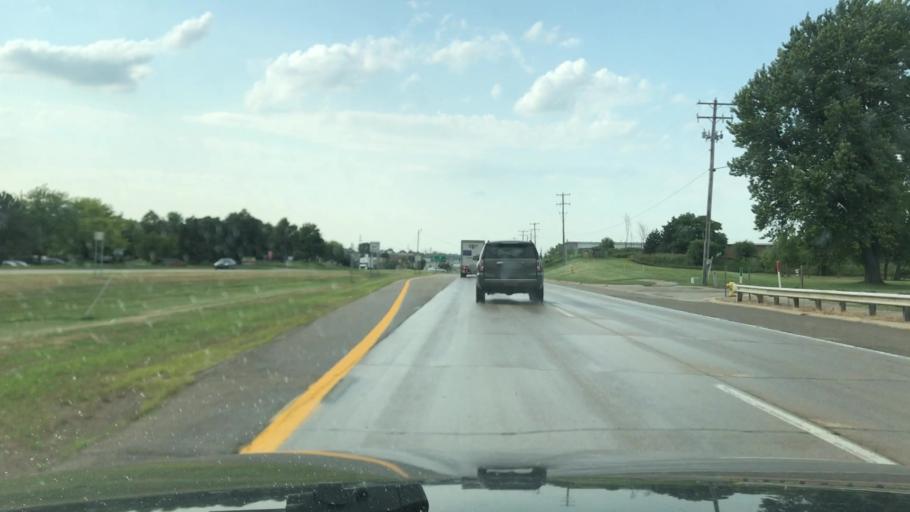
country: US
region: Michigan
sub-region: Kent County
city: East Grand Rapids
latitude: 42.8804
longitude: -85.5625
